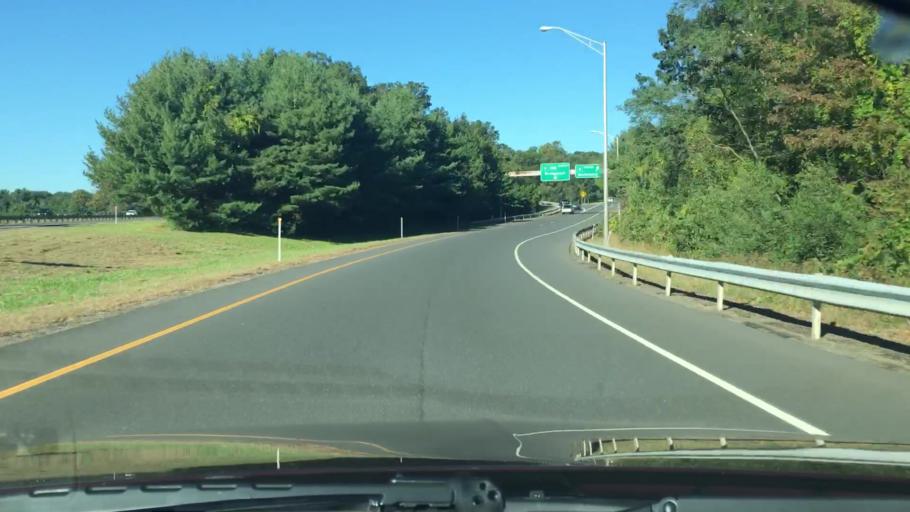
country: US
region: Connecticut
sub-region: Fairfield County
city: Trumbull
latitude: 41.2372
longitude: -73.1468
